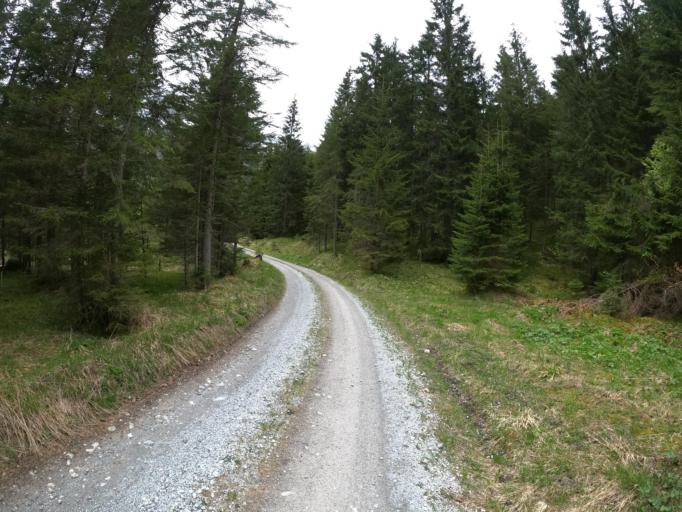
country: AT
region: Salzburg
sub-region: Politischer Bezirk Zell am See
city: Dienten am Hochkonig
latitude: 47.4661
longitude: 13.0537
